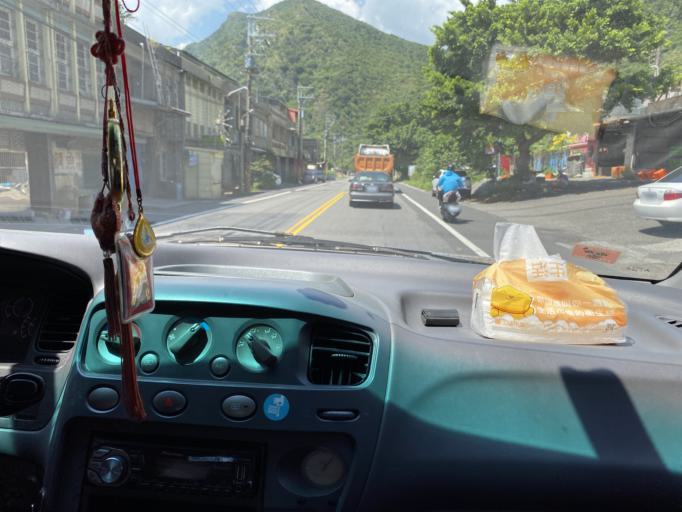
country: TW
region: Taiwan
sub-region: Yilan
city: Yilan
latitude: 24.9419
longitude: 121.8981
